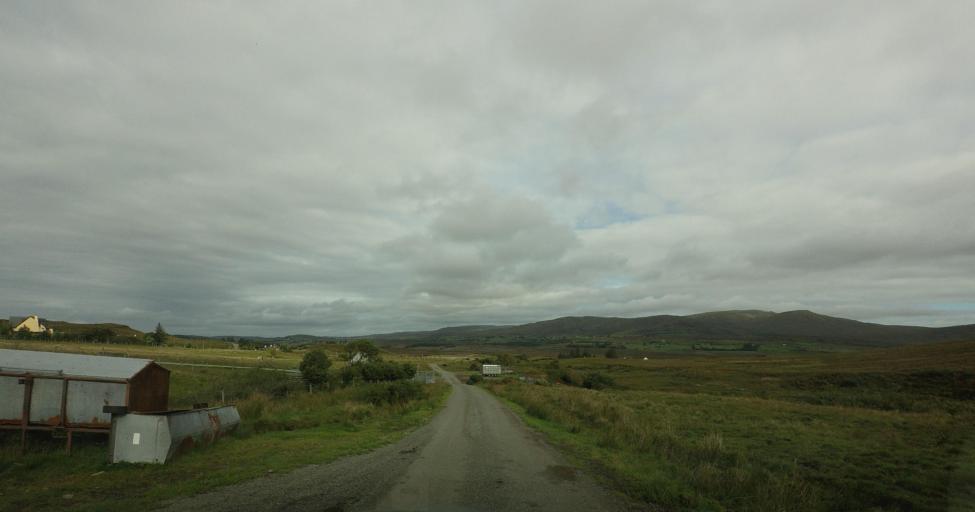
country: GB
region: Scotland
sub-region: Highland
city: Isle of Skye
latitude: 57.4181
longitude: -6.2570
